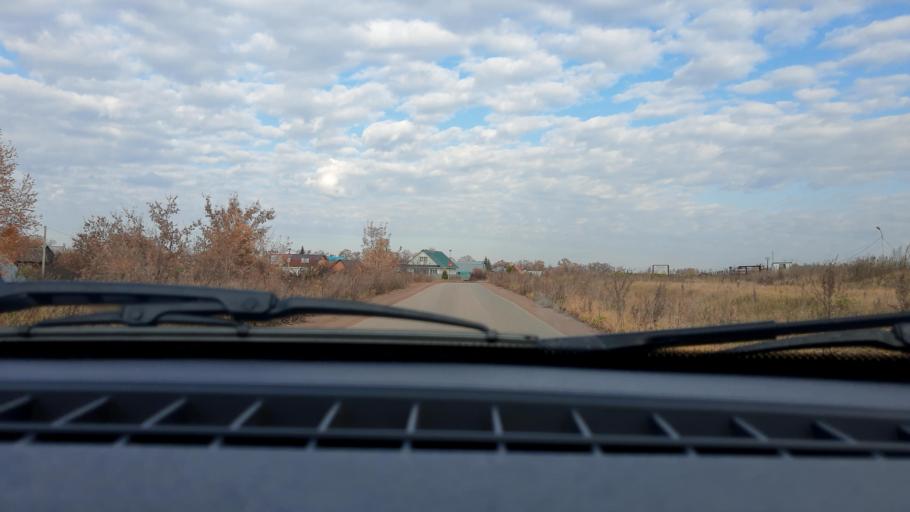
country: RU
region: Bashkortostan
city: Ufa
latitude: 54.5989
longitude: 55.8980
